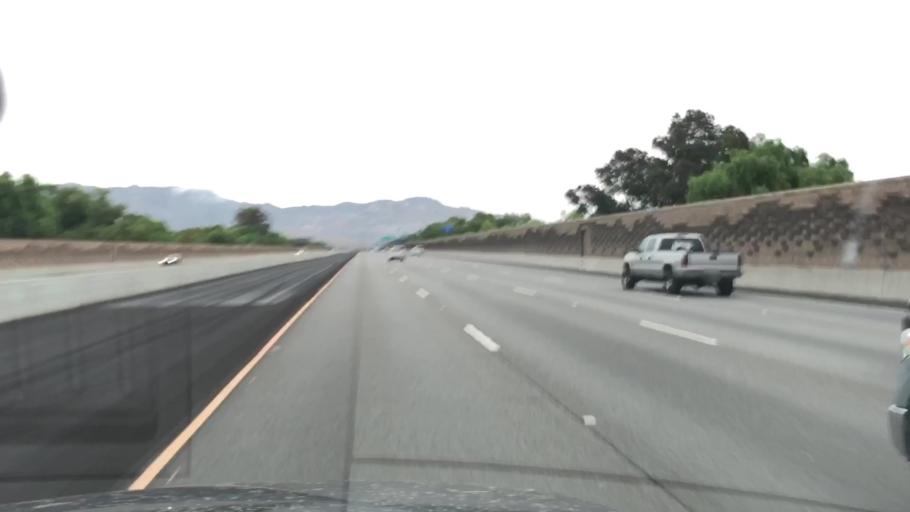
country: US
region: California
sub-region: Ventura County
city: Santa Susana
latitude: 34.2816
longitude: -118.7054
